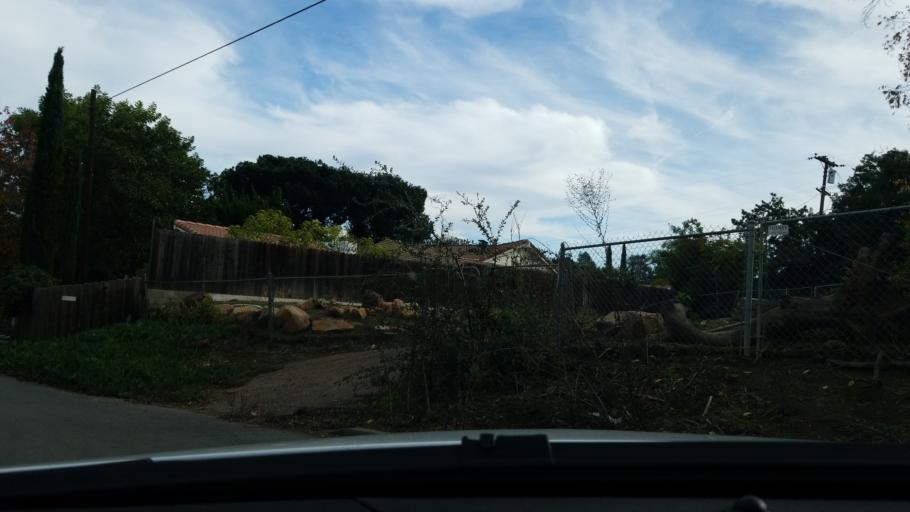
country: US
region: California
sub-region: San Diego County
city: Casa de Oro-Mount Helix
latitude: 32.7732
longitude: -116.9473
